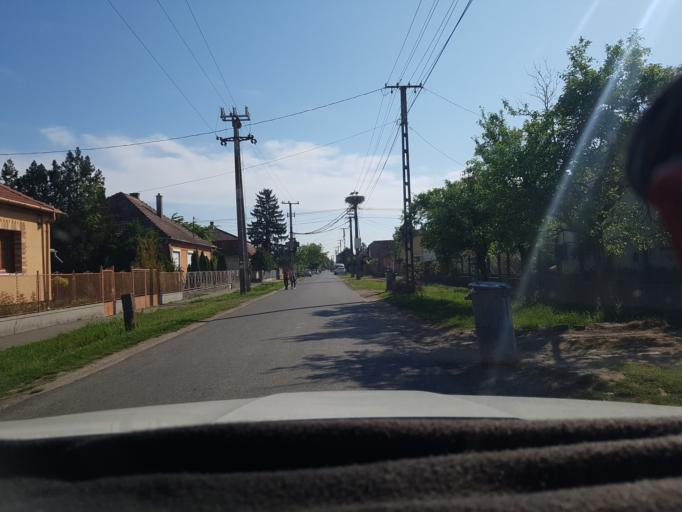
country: HU
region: Tolna
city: Decs
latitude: 46.2807
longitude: 18.7522
